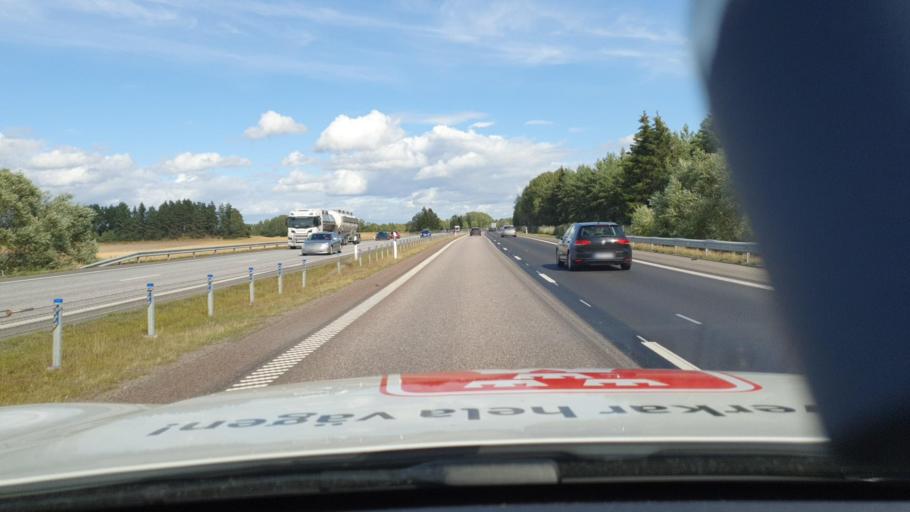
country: SE
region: OEstergoetland
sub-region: Linkopings Kommun
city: Linghem
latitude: 58.4764
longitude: 15.8423
